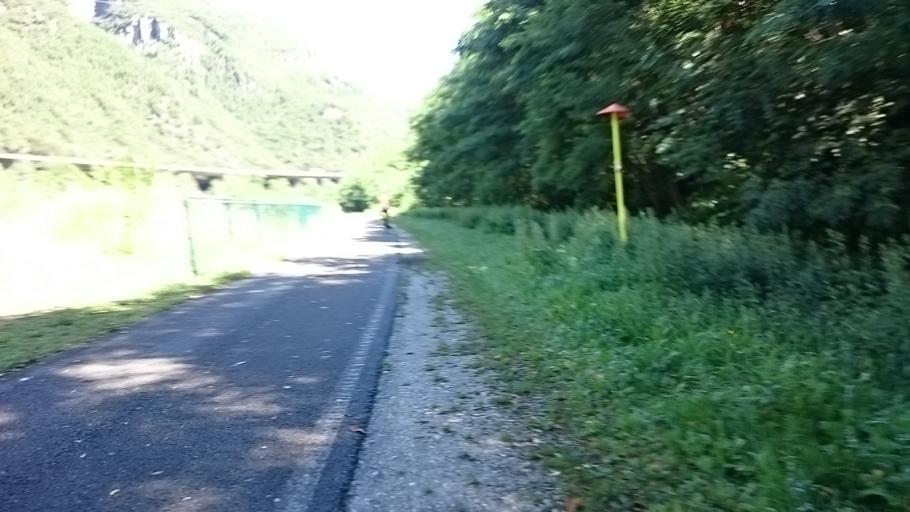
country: IT
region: Trentino-Alto Adige
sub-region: Bolzano
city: Collalbo
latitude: 46.5020
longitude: 11.4589
